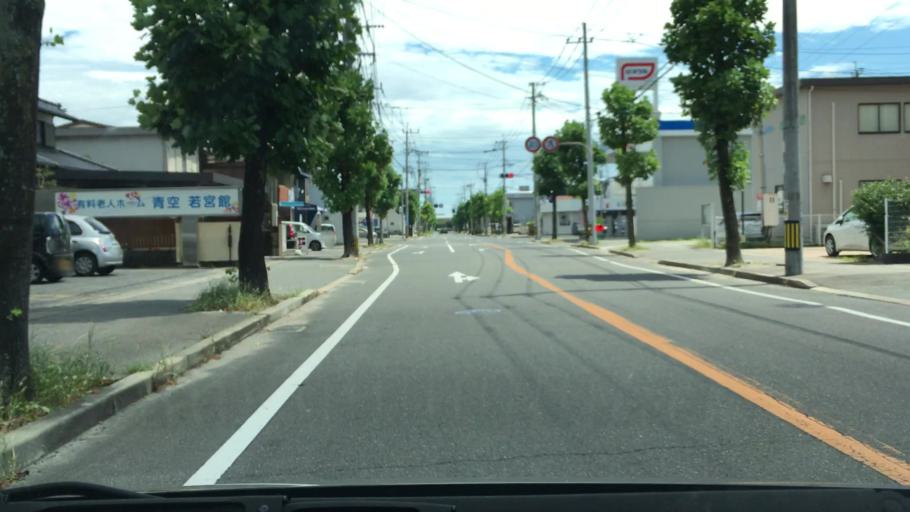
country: JP
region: Saga Prefecture
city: Saga-shi
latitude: 33.2707
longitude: 130.2868
